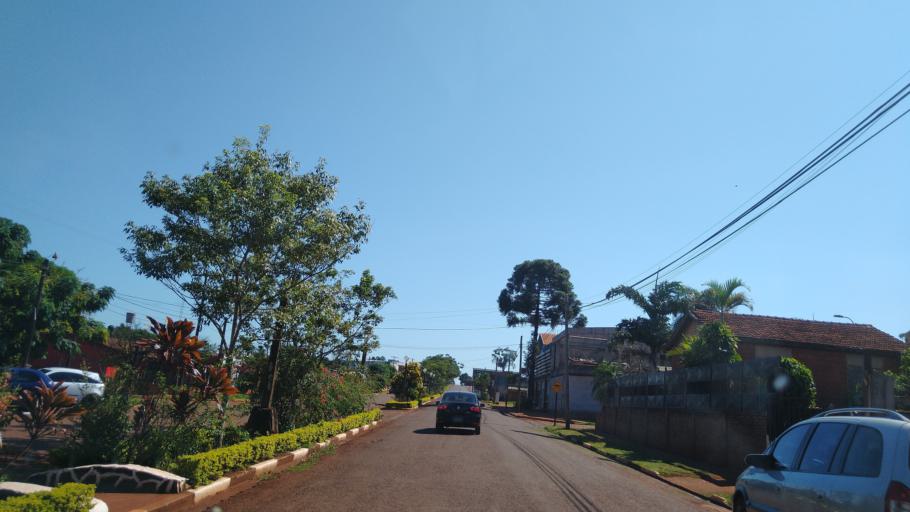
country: AR
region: Misiones
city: Puerto Libertad
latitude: -25.9684
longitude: -54.5606
